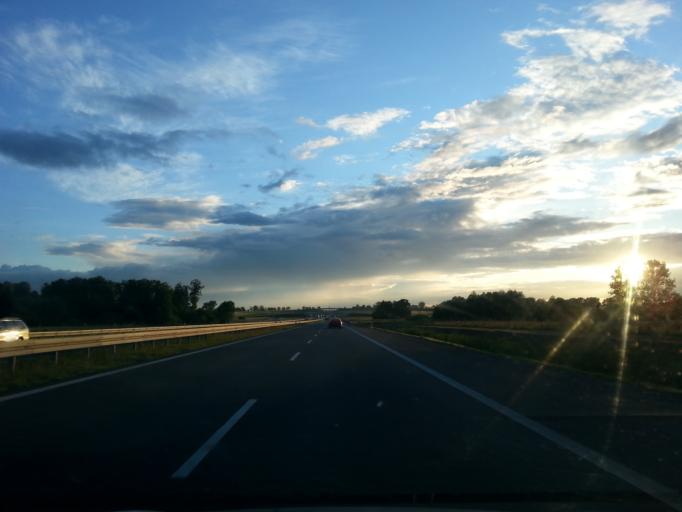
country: PL
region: Lower Silesian Voivodeship
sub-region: Powiat olesnicki
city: Sycow
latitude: 51.2941
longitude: 17.7055
